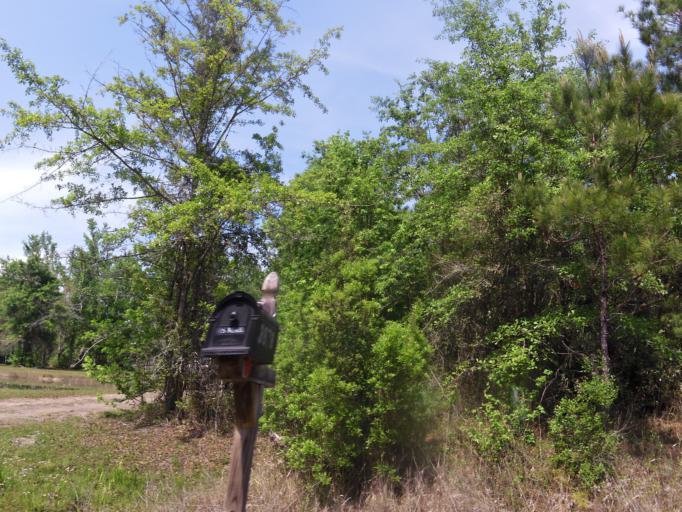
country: US
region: Georgia
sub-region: Camden County
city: Kingsland
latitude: 30.8035
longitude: -81.7380
